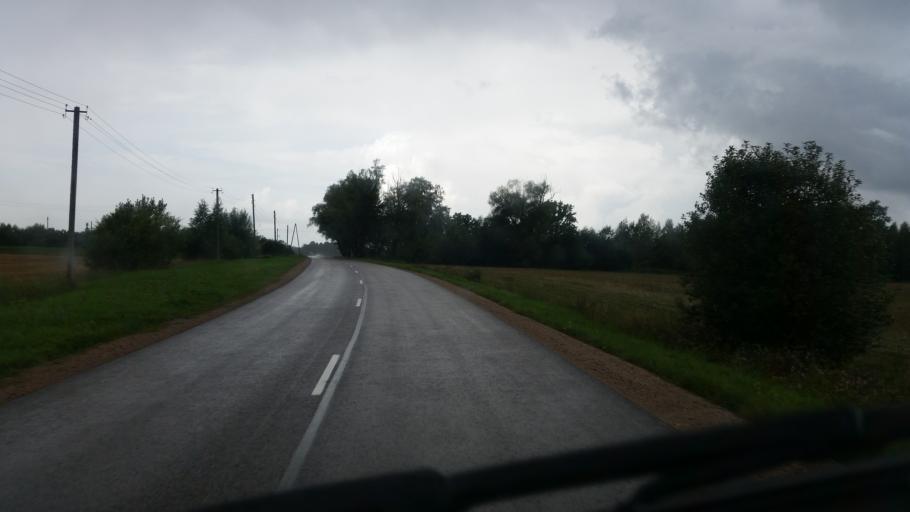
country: LV
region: Vecumnieki
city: Vecumnieki
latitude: 56.4328
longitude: 24.4137
